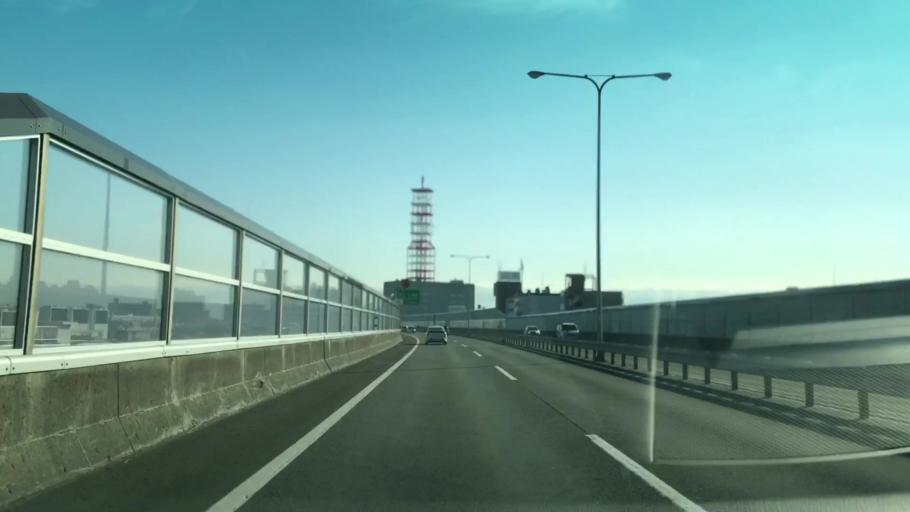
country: JP
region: Hokkaido
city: Sapporo
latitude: 43.1010
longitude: 141.3283
